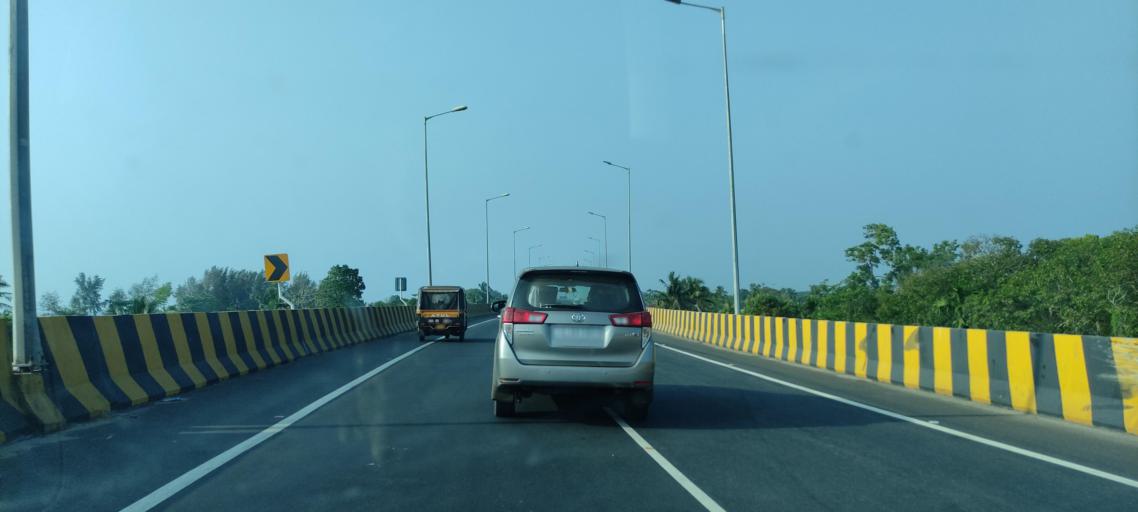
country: IN
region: Kerala
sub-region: Alappuzha
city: Alleppey
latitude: 9.4799
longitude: 76.3222
